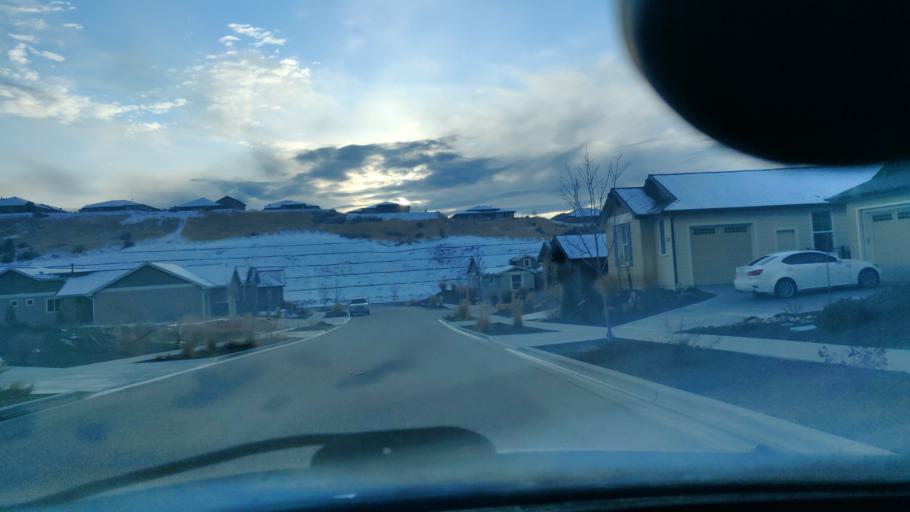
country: US
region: Idaho
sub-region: Ada County
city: Eagle
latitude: 43.7734
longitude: -116.2536
